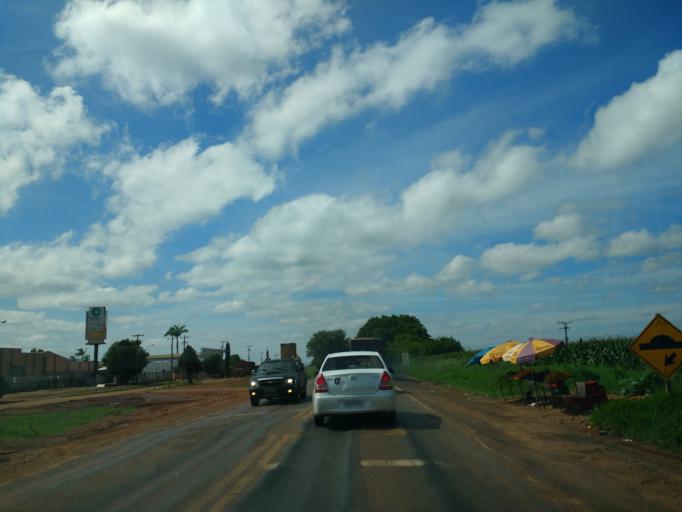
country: BR
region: Parana
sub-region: Terra Boa
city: Terra Boa
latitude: -23.6318
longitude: -52.4631
